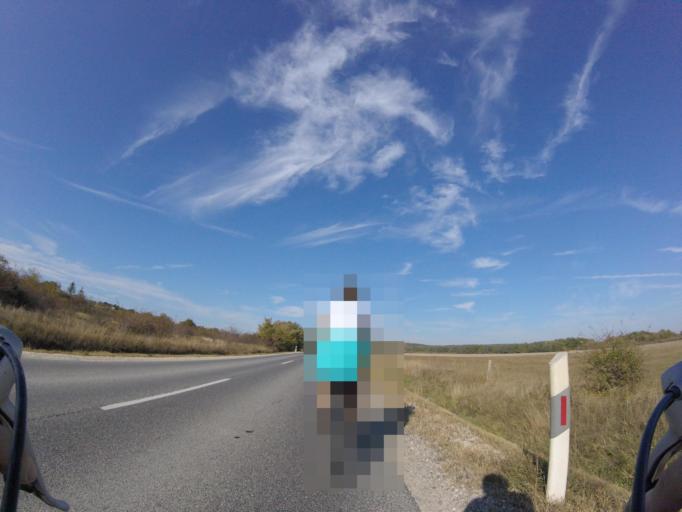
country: HU
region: Fejer
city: Zamoly
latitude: 47.3506
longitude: 18.4008
